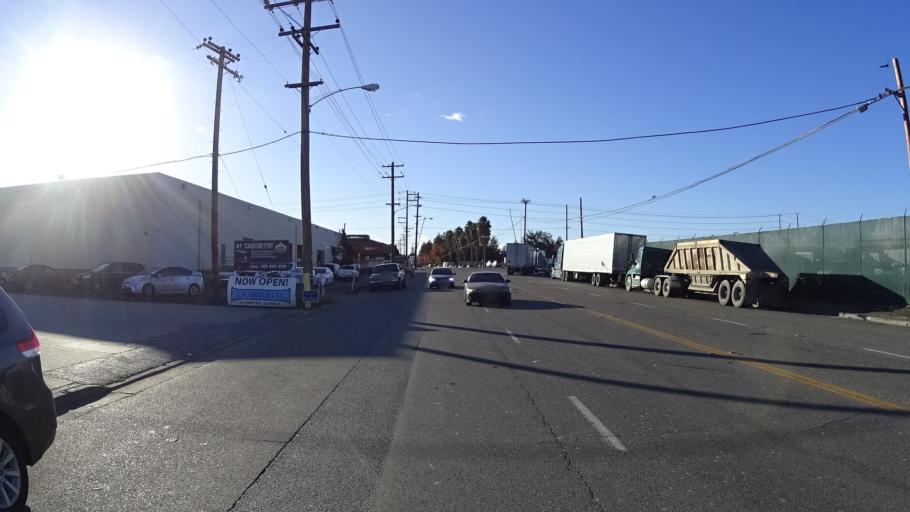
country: US
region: California
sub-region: Santa Clara County
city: Santa Clara
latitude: 37.3665
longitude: -121.9443
